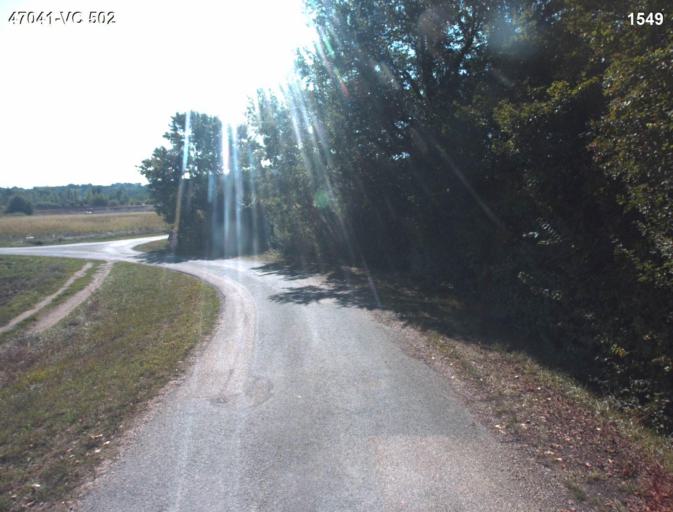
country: FR
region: Aquitaine
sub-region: Departement du Lot-et-Garonne
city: Port-Sainte-Marie
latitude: 44.2189
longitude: 0.3911
